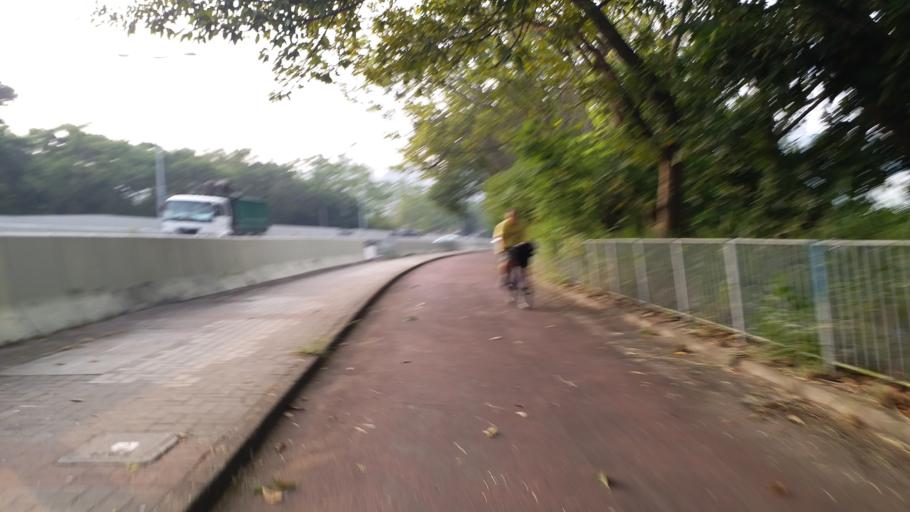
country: HK
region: Yuen Long
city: Yuen Long Kau Hui
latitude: 22.4475
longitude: 114.0127
